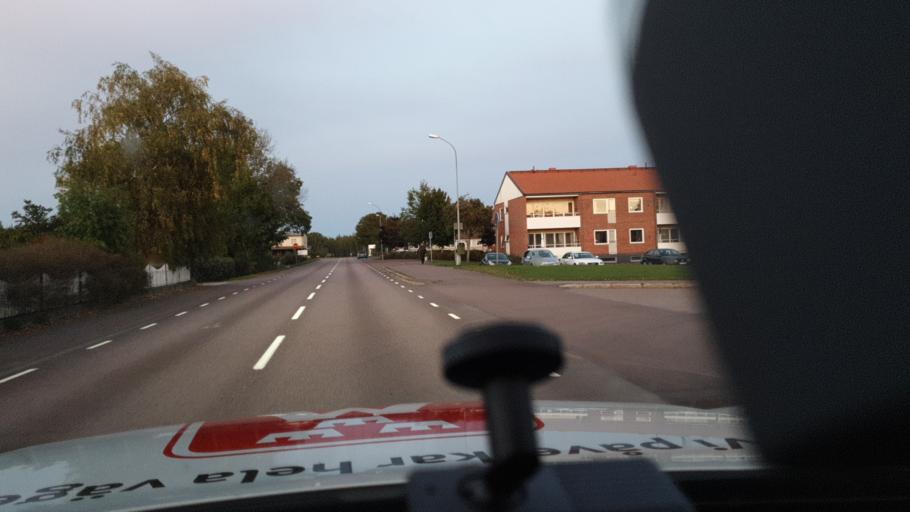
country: SE
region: Kalmar
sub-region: Monsteras Kommun
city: Blomstermala
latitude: 57.1274
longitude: 16.2614
